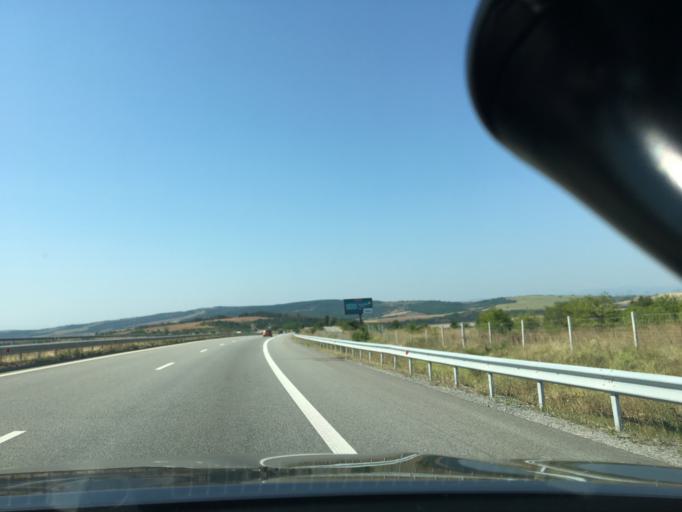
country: BG
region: Kyustendil
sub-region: Obshtina Bobovdol
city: Bobovdol
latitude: 42.3530
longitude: 23.0987
